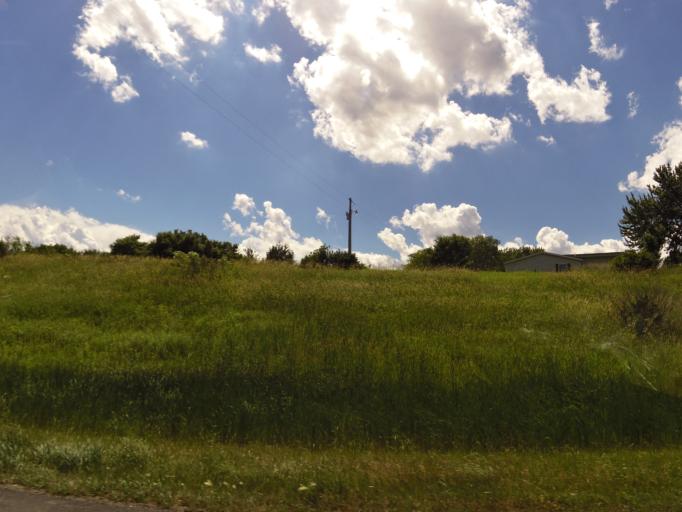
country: US
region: Iowa
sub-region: Linn County
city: Ely
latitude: 41.8336
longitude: -91.6627
